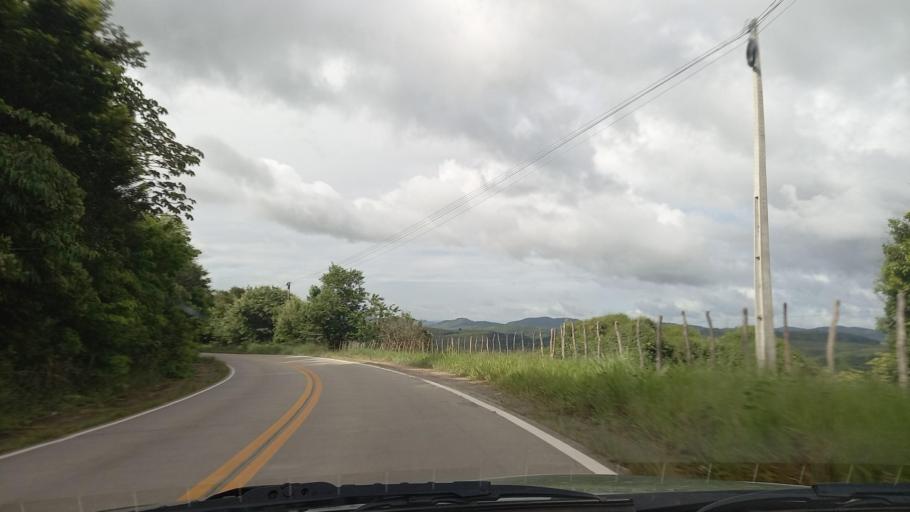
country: BR
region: Pernambuco
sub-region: Maraial
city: Maraial
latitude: -8.7830
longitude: -35.8740
